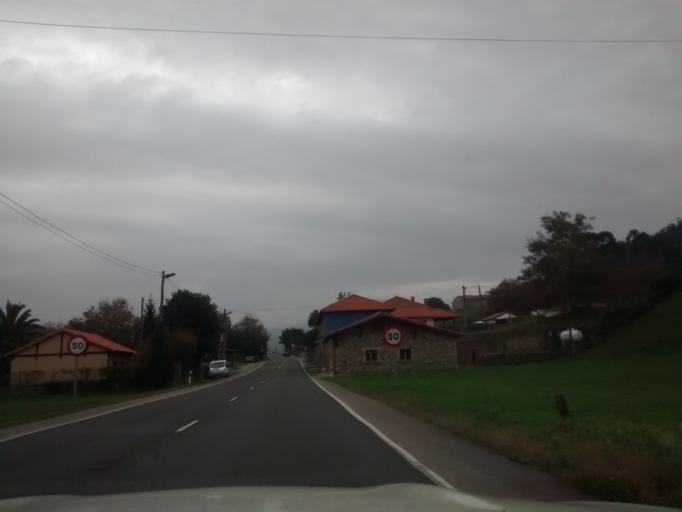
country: ES
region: Cantabria
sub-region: Provincia de Cantabria
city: Puente Viesgo
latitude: 43.2852
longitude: -3.9538
